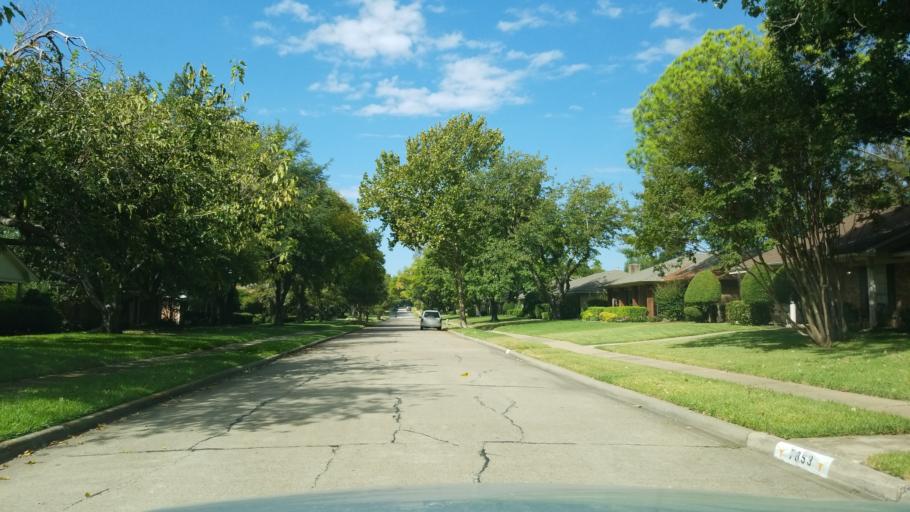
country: US
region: Texas
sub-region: Dallas County
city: Richardson
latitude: 32.9695
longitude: -96.7702
